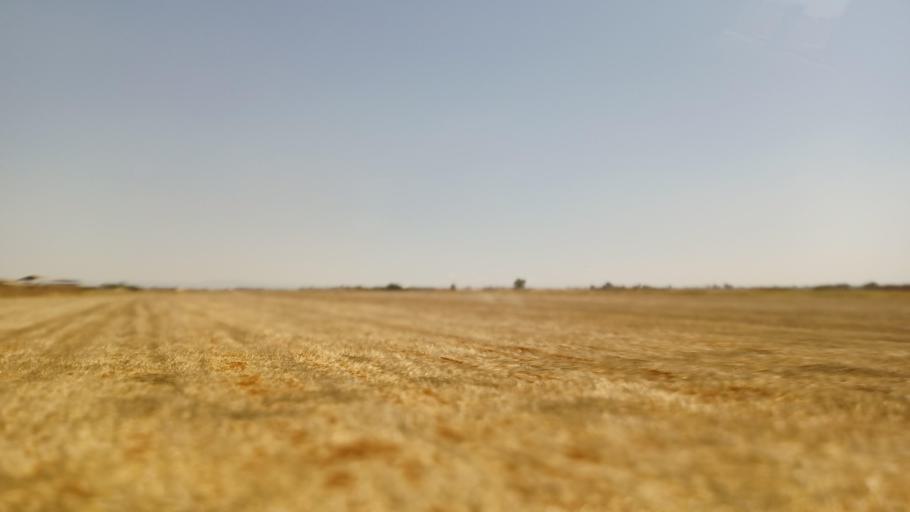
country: CY
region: Ammochostos
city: Avgorou
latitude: 35.0262
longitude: 33.8144
